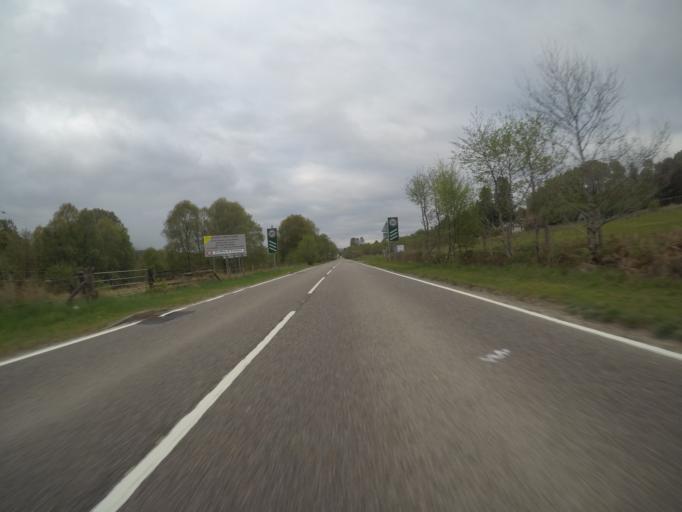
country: GB
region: Scotland
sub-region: Highland
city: Spean Bridge
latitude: 56.8953
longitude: -4.9061
